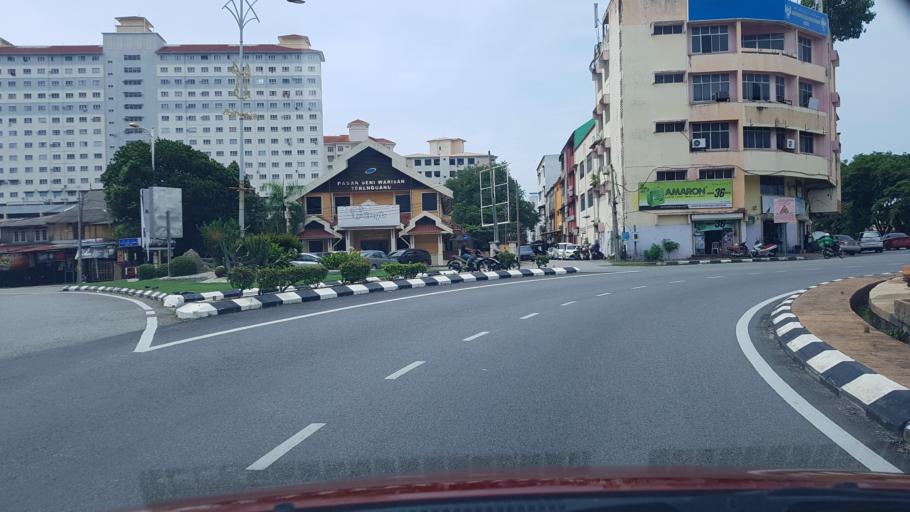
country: MY
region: Terengganu
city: Kuala Terengganu
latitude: 5.3290
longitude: 103.1458
